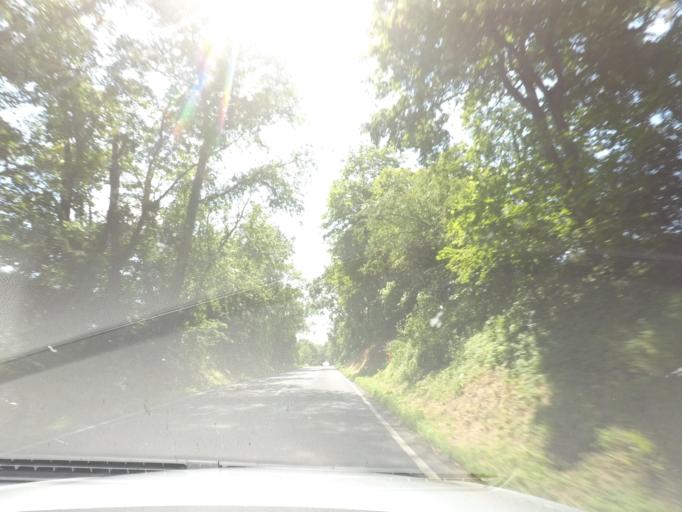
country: DE
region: Saxony-Anhalt
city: Haldensleben I
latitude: 52.2561
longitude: 11.4149
